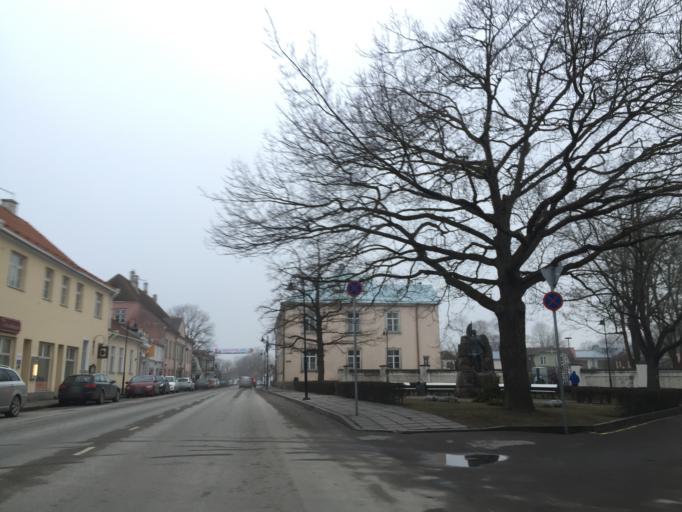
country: EE
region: Saare
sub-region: Kuressaare linn
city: Kuressaare
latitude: 58.2525
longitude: 22.4849
